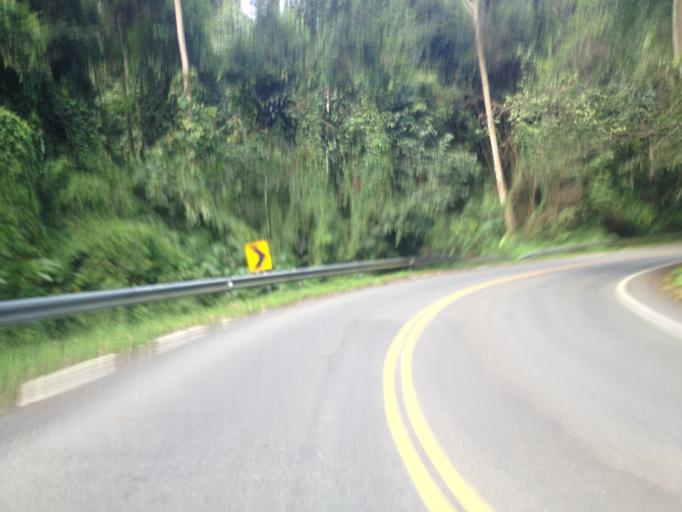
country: TH
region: Chiang Mai
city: Chiang Mai
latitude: 18.8053
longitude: 98.9088
